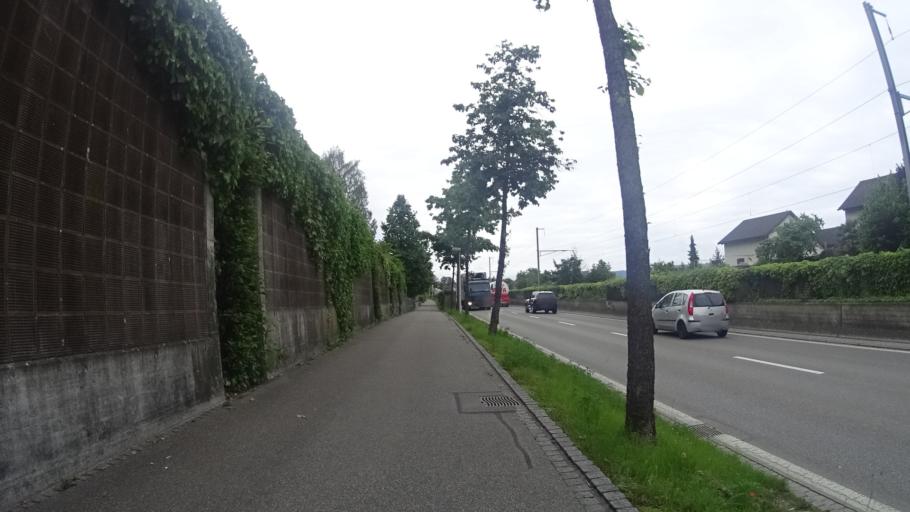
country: CH
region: Aargau
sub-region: Bezirk Zurzach
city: Klingnau
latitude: 47.5666
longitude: 8.2561
